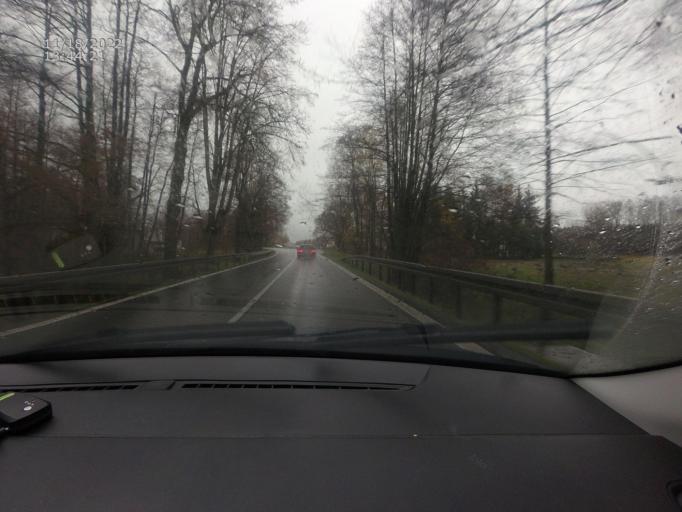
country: CZ
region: Jihocesky
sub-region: Okres Strakonice
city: Blatna
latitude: 49.4301
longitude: 13.8272
